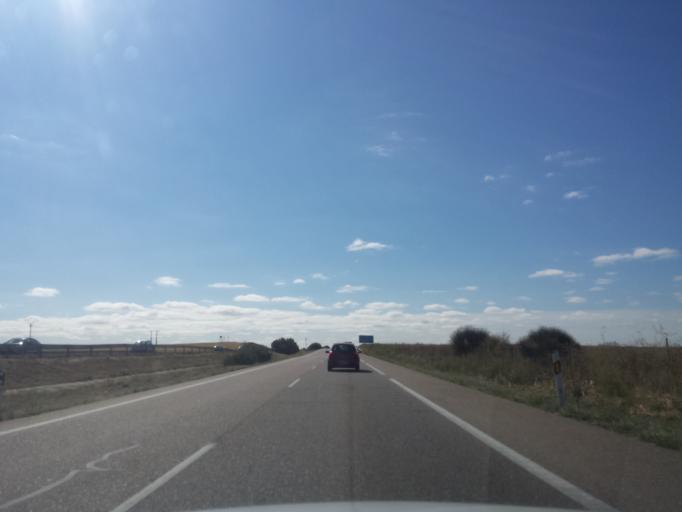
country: ES
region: Castille and Leon
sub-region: Provincia de Zamora
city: San Esteban del Molar
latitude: 41.9516
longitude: -5.5685
